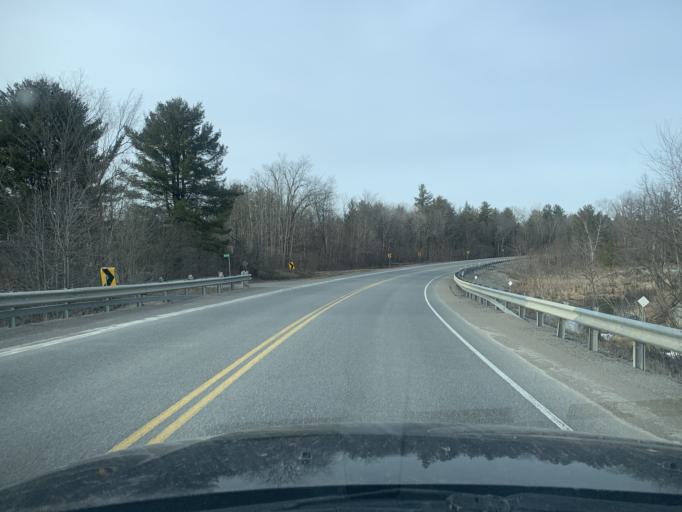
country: CA
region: Ontario
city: Greater Napanee
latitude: 44.5751
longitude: -77.1182
